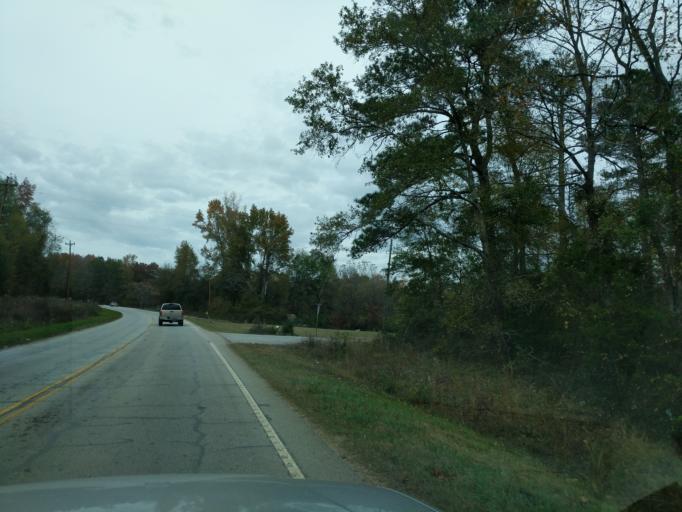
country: US
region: South Carolina
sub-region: Newberry County
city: Newberry
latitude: 34.2758
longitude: -81.6375
